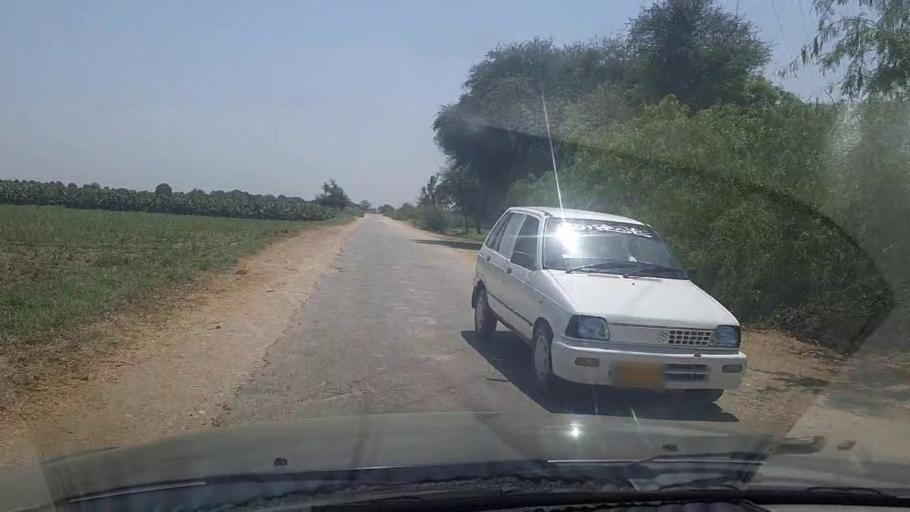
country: PK
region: Sindh
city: Tando Jam
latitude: 25.2762
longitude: 68.6201
